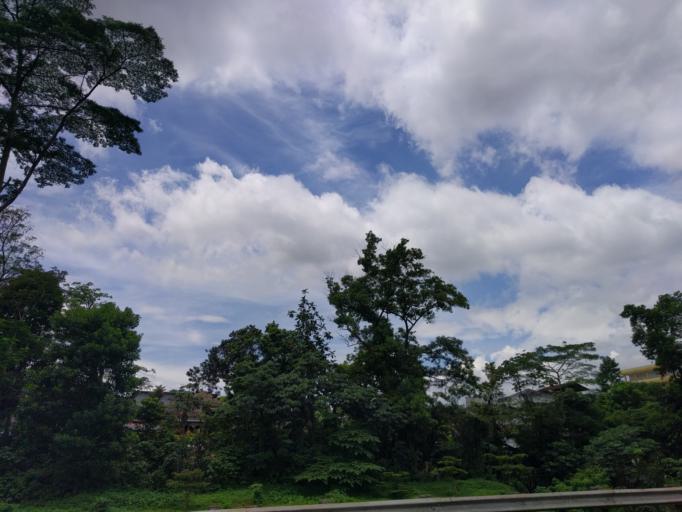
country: ID
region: West Java
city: Bogor
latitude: -6.6025
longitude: 106.8101
